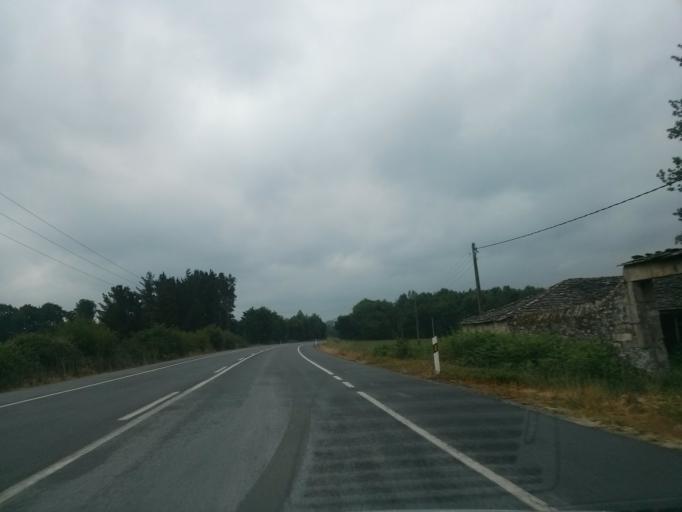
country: ES
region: Galicia
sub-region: Provincia de Lugo
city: Begonte
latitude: 43.1633
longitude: -7.7044
